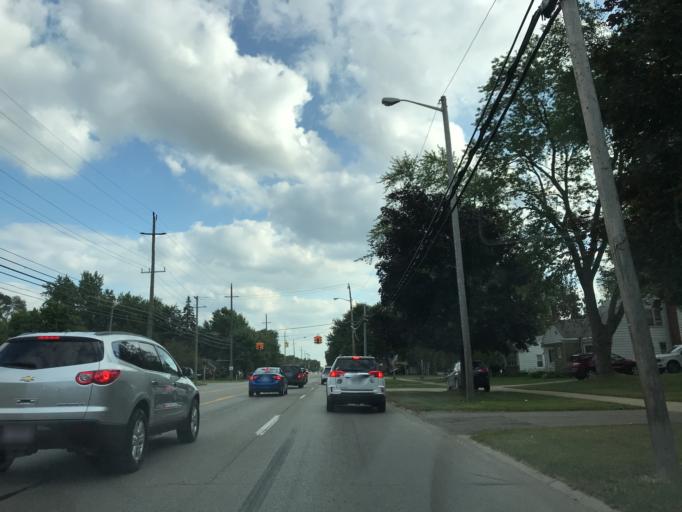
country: US
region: Michigan
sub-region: Wayne County
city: Redford
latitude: 42.3905
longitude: -83.2956
